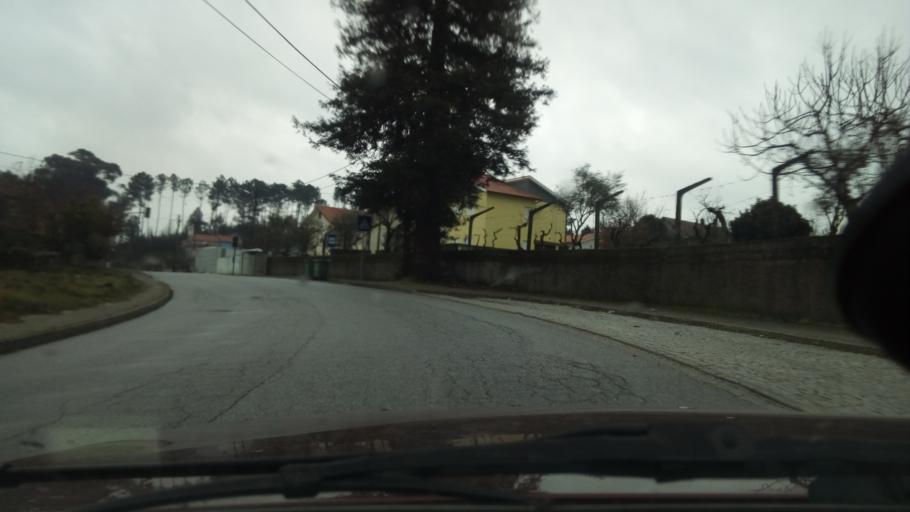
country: PT
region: Viseu
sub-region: Mangualde
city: Mangualde
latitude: 40.6263
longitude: -7.8073
